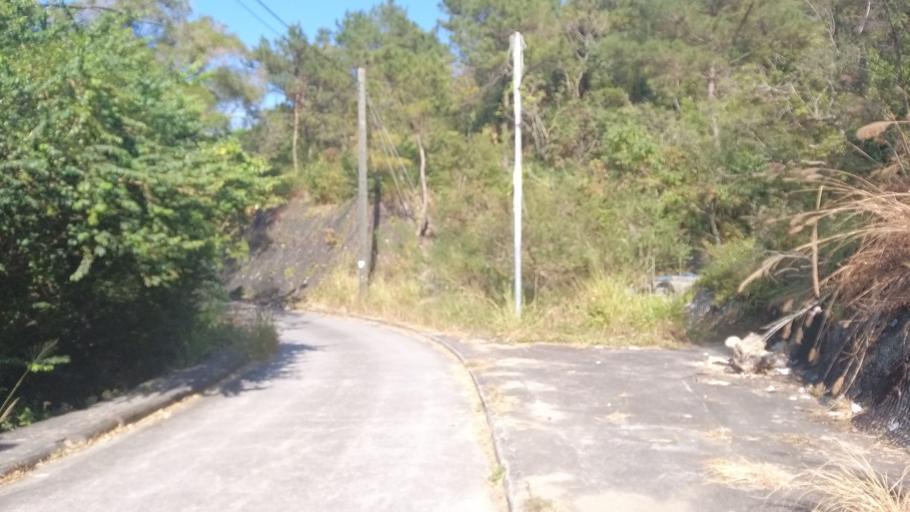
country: HK
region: Tuen Mun
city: Tuen Mun
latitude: 22.4055
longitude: 113.9867
